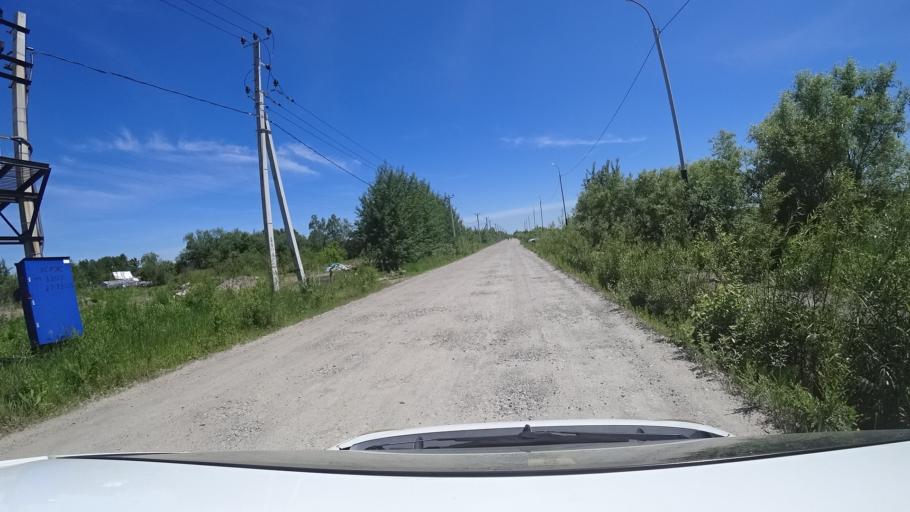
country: RU
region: Khabarovsk Krai
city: Topolevo
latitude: 48.5013
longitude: 135.1890
